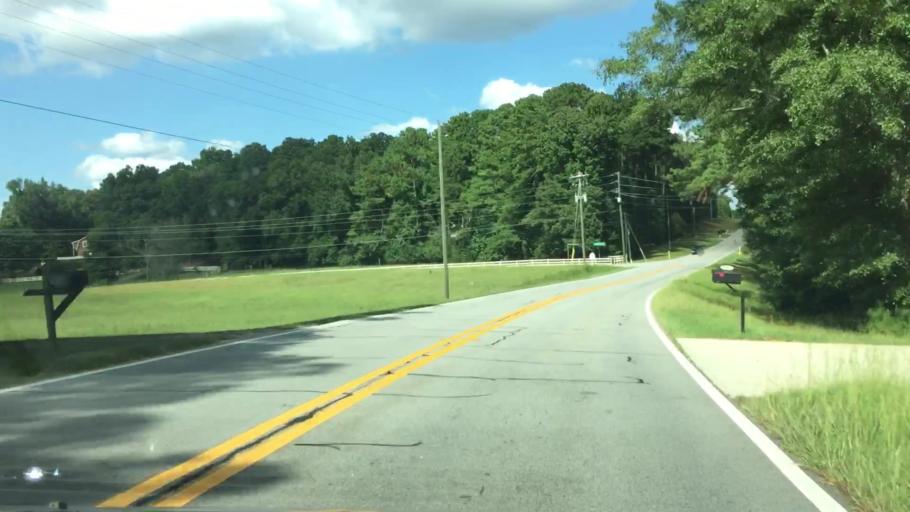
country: US
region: Georgia
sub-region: Fayette County
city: Shannon
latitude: 33.4076
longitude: -84.4918
